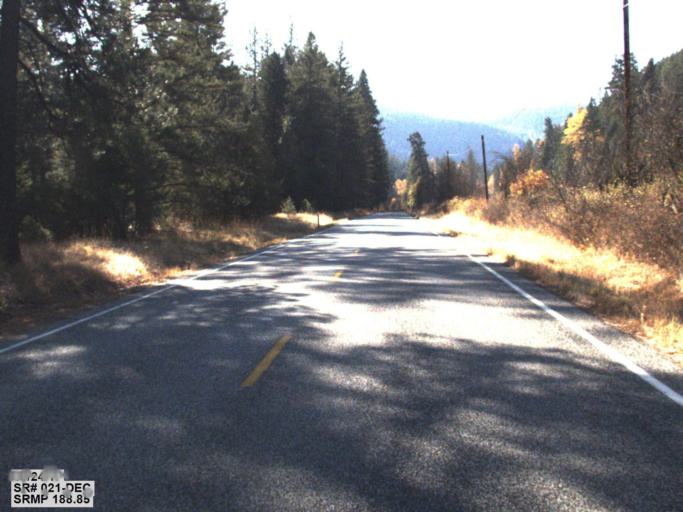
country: CA
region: British Columbia
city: Grand Forks
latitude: 48.9709
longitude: -118.5270
